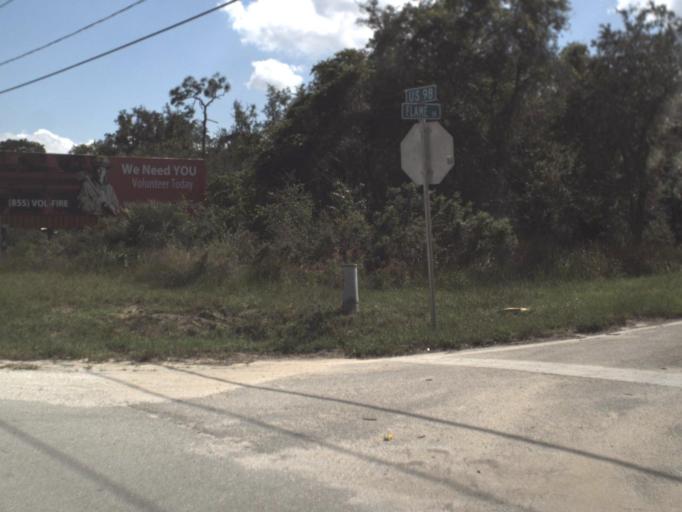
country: US
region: Florida
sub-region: Highlands County
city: Sebring
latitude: 27.4282
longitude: -81.4127
